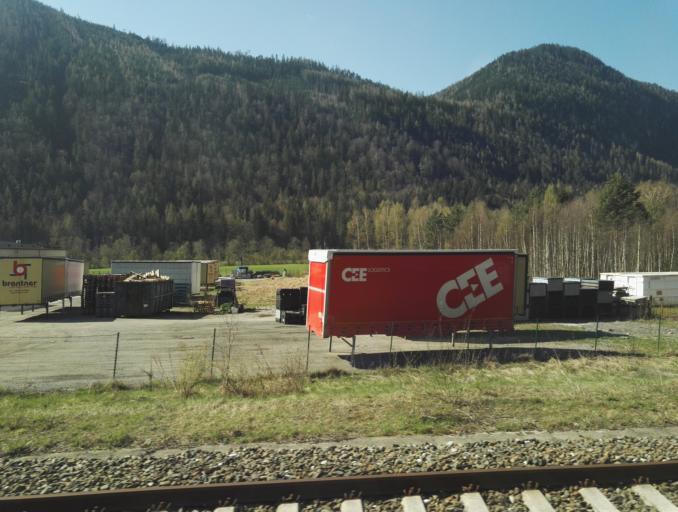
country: AT
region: Salzburg
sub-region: Politischer Bezirk Sankt Johann im Pongau
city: Forstau
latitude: 47.4039
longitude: 13.5688
